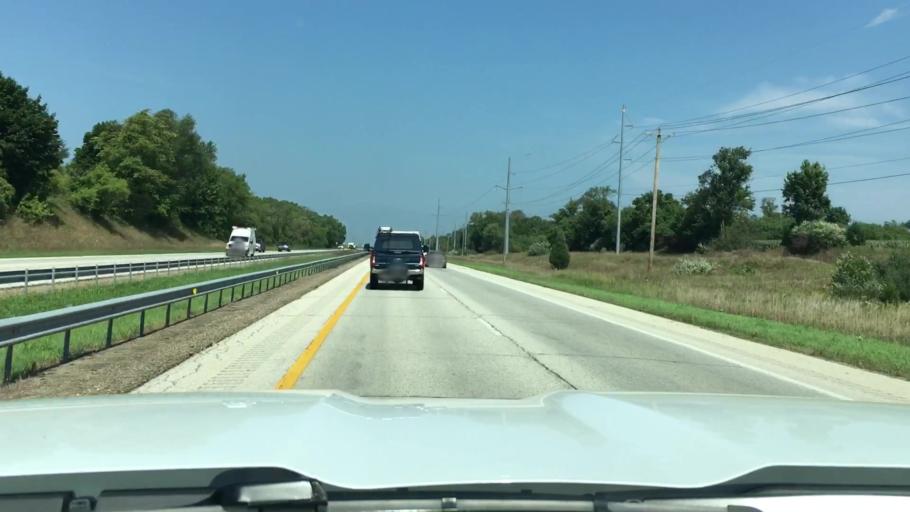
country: US
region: Michigan
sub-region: Kalamazoo County
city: Schoolcraft
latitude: 42.0581
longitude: -85.6359
